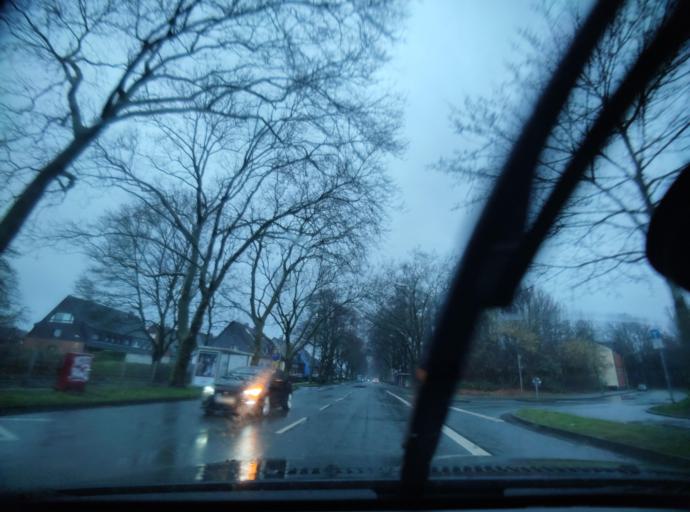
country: DE
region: North Rhine-Westphalia
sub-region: Regierungsbezirk Dusseldorf
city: Essen
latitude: 51.4839
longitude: 7.0298
